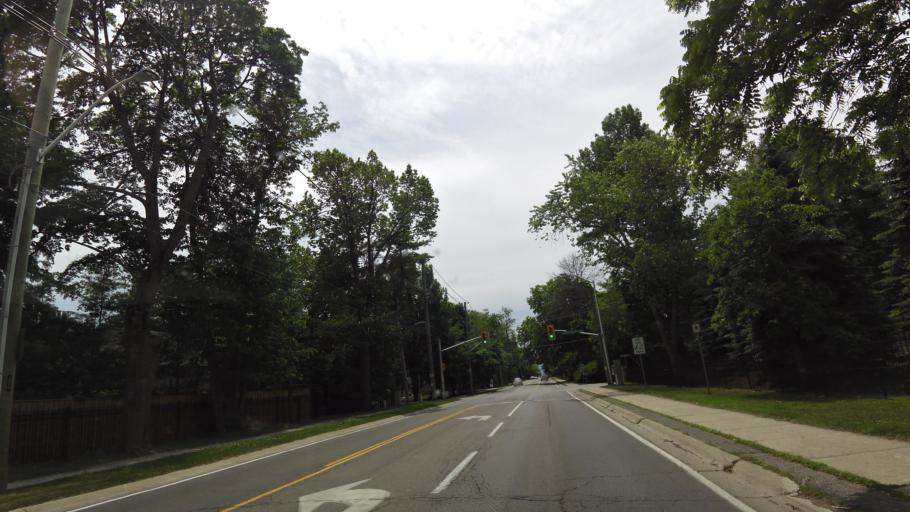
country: CA
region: Ontario
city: Oakville
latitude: 43.4546
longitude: -79.6587
